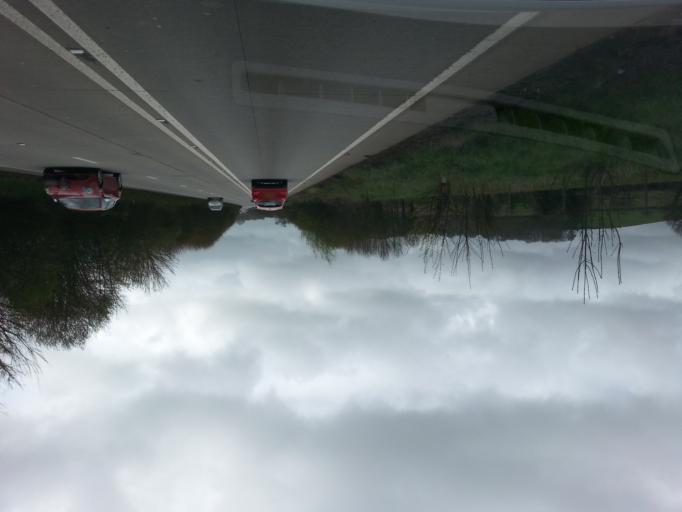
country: GB
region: England
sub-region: Somerset
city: Ilminster
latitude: 50.9404
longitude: -2.8854
